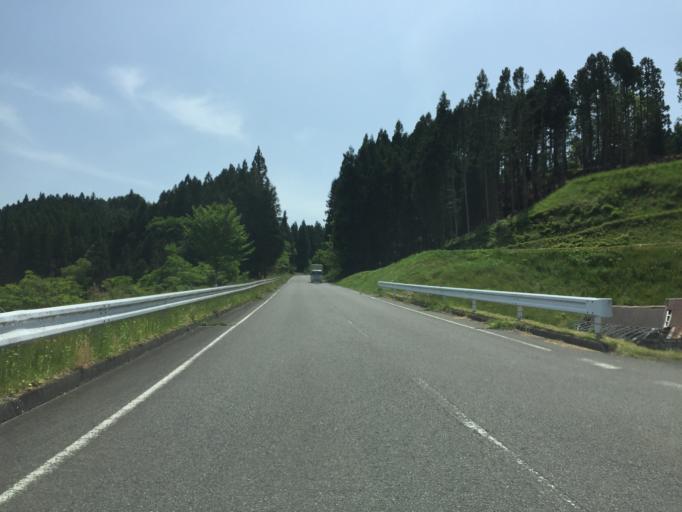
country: JP
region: Fukushima
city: Ishikawa
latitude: 37.1788
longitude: 140.5091
